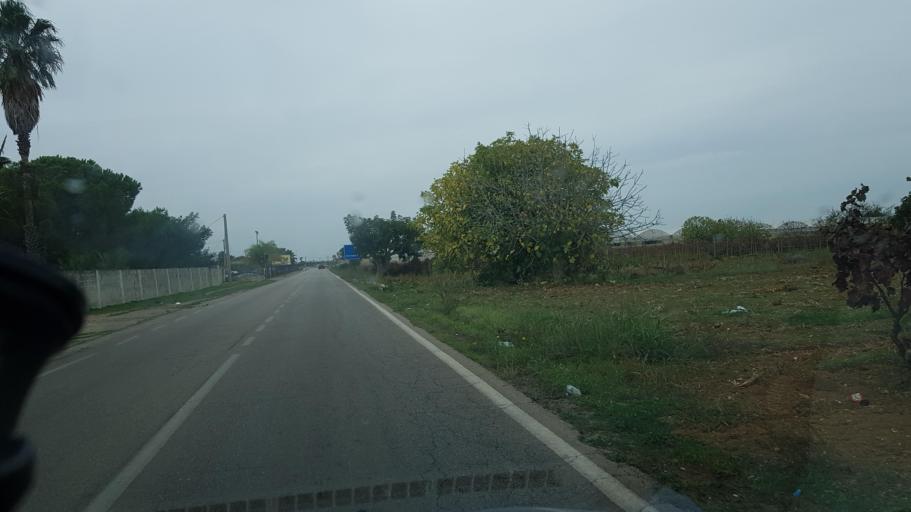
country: IT
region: Apulia
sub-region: Provincia di Lecce
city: Leverano
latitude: 40.3033
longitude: 17.9923
